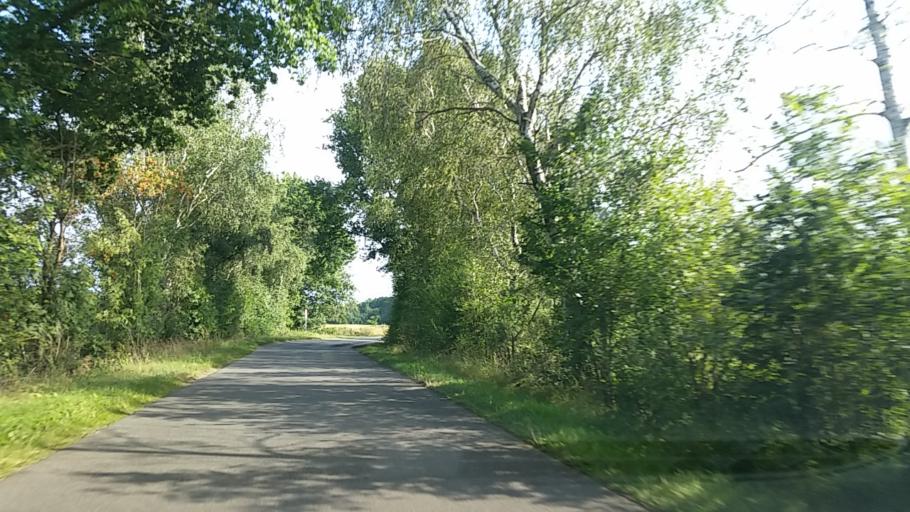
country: DE
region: Lower Saxony
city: Radbruch
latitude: 53.3268
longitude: 10.2436
